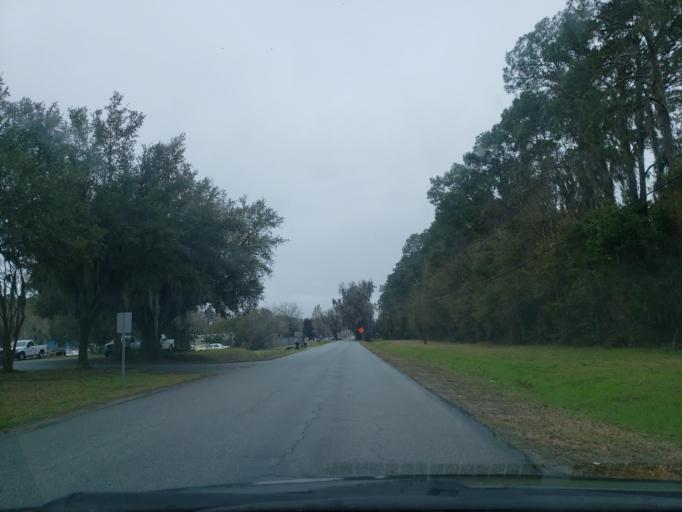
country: US
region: Georgia
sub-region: Chatham County
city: Isle of Hope
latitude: 32.0074
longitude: -81.0907
